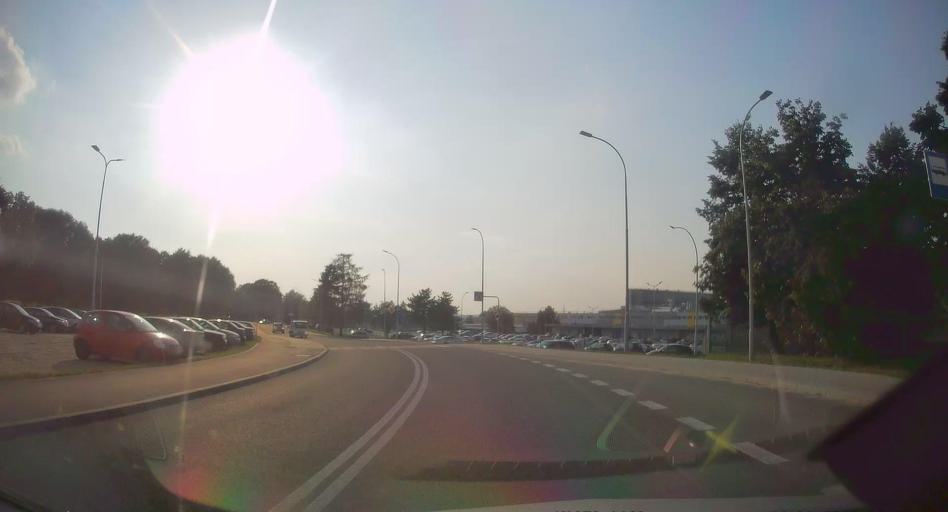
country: PL
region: Subcarpathian Voivodeship
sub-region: Powiat debicki
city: Debica
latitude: 50.0406
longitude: 21.3881
